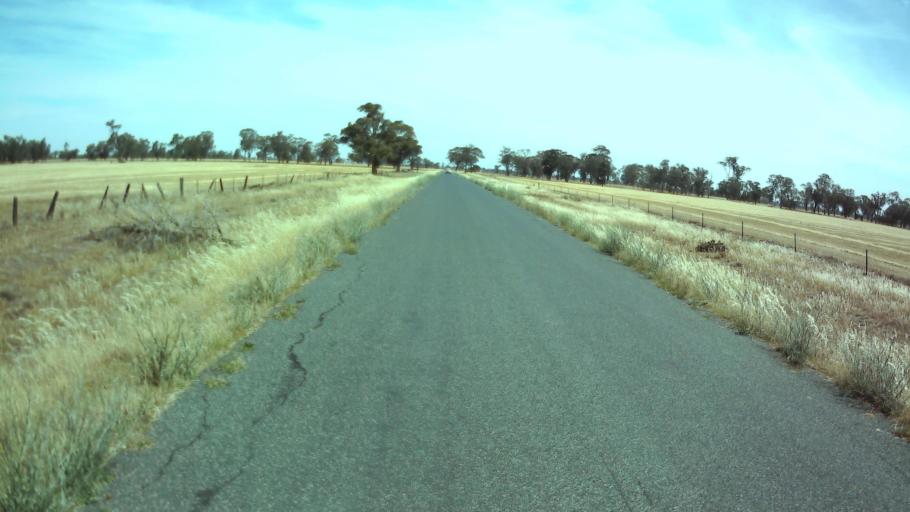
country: AU
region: New South Wales
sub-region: Weddin
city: Grenfell
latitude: -34.0014
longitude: 147.7740
